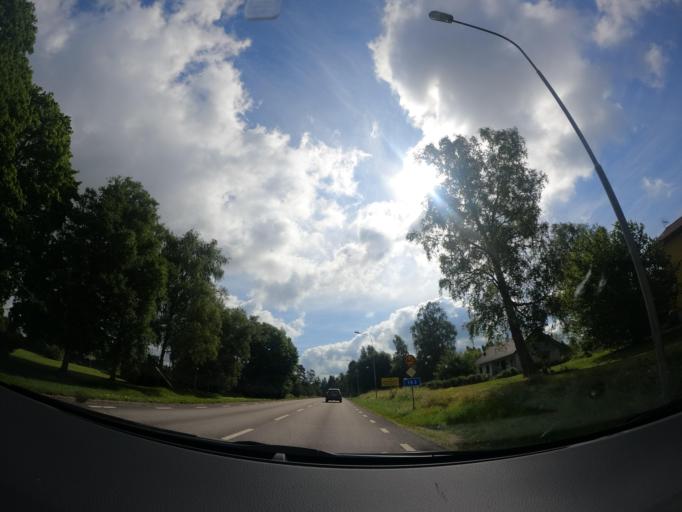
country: SE
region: Halland
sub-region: Hylte Kommun
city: Torup
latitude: 57.1054
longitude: 13.0388
